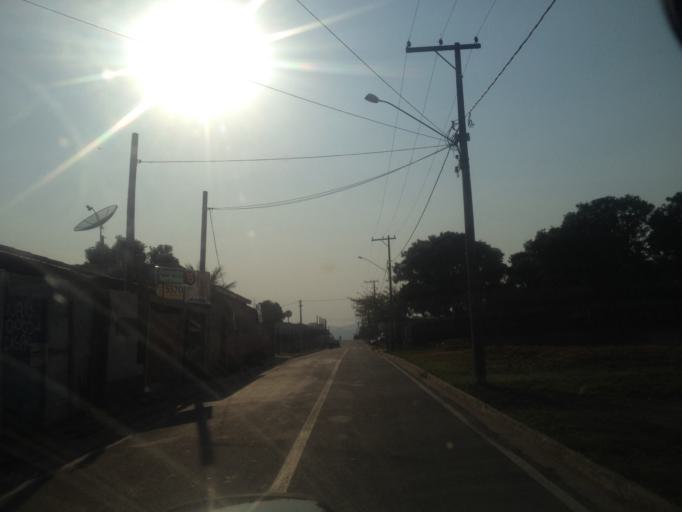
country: BR
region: Rio de Janeiro
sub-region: Porto Real
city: Porto Real
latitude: -22.4411
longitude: -44.3250
